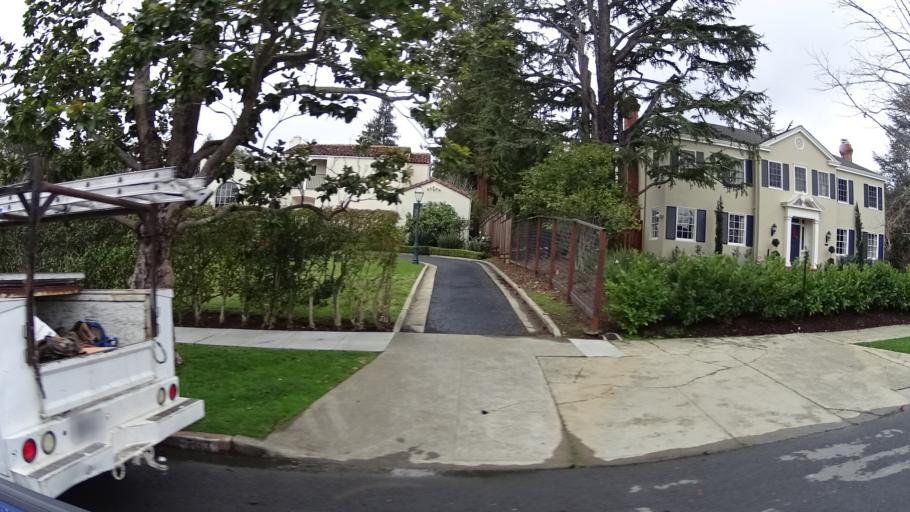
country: US
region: California
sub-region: San Mateo County
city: Burlingame
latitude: 37.5695
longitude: -122.3521
